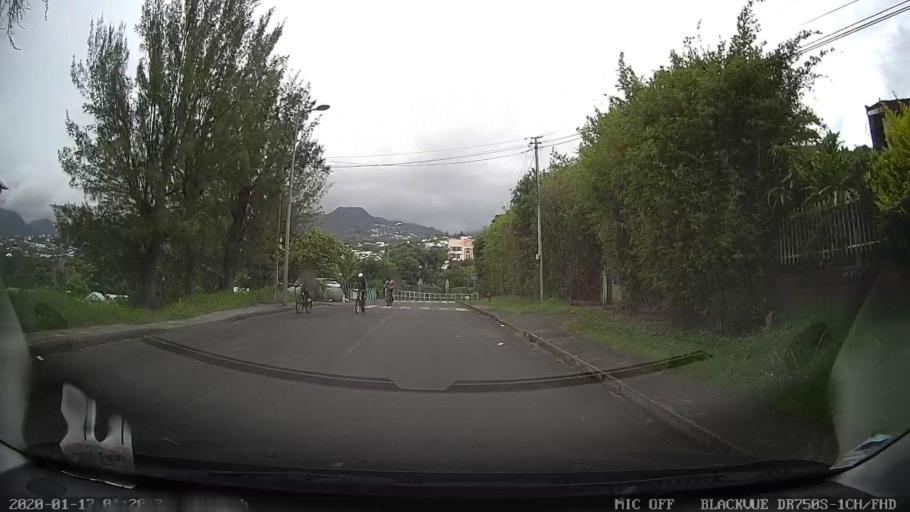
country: RE
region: Reunion
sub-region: Reunion
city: Saint-Denis
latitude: -20.9107
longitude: 55.4869
